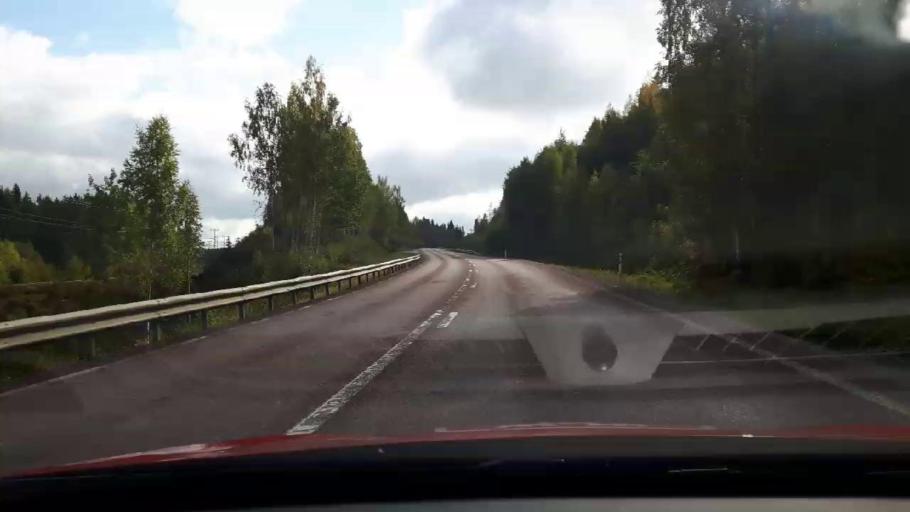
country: SE
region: Gaevleborg
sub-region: Ljusdals Kommun
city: Jaervsoe
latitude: 61.6219
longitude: 16.2866
